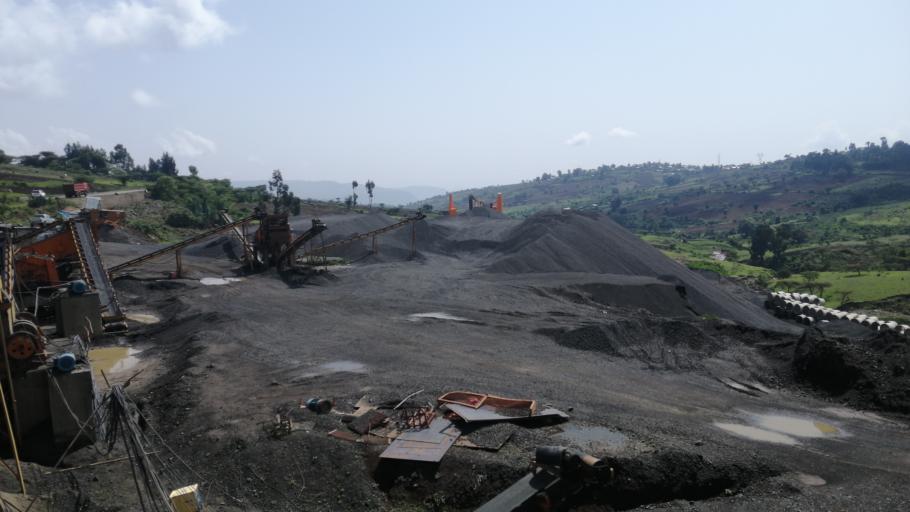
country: ET
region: Oromiya
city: Guder
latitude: 8.9793
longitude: 37.6285
